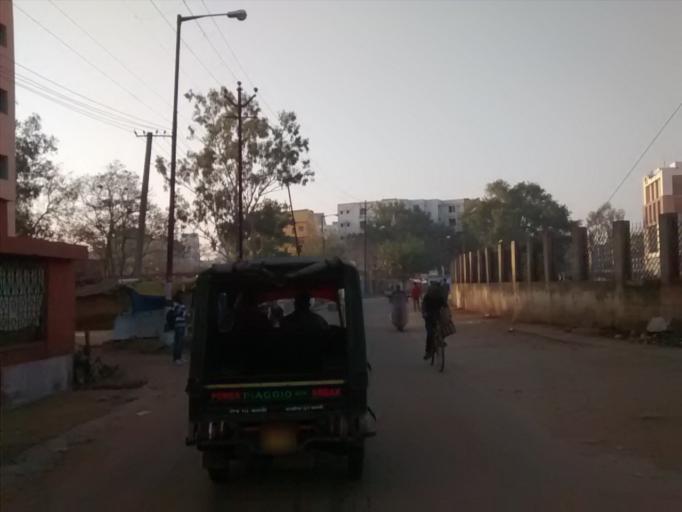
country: IN
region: Jharkhand
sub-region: Ranchi
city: Ranchi
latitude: 23.3735
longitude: 85.3272
